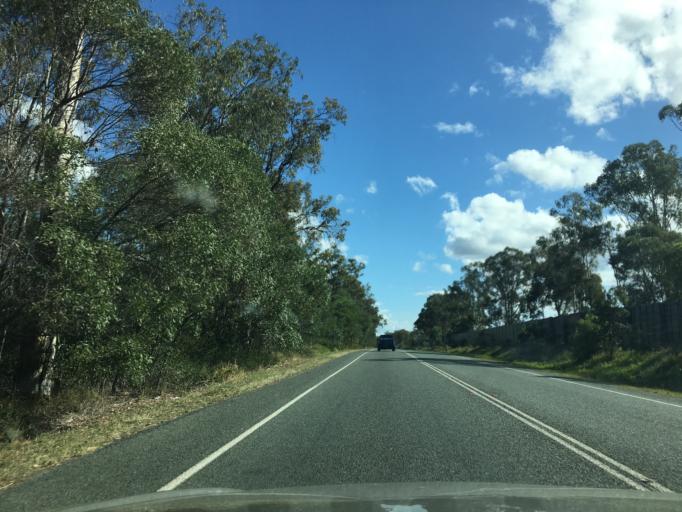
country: AU
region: Queensland
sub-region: Logan
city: Chambers Flat
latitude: -27.7734
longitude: 153.1045
